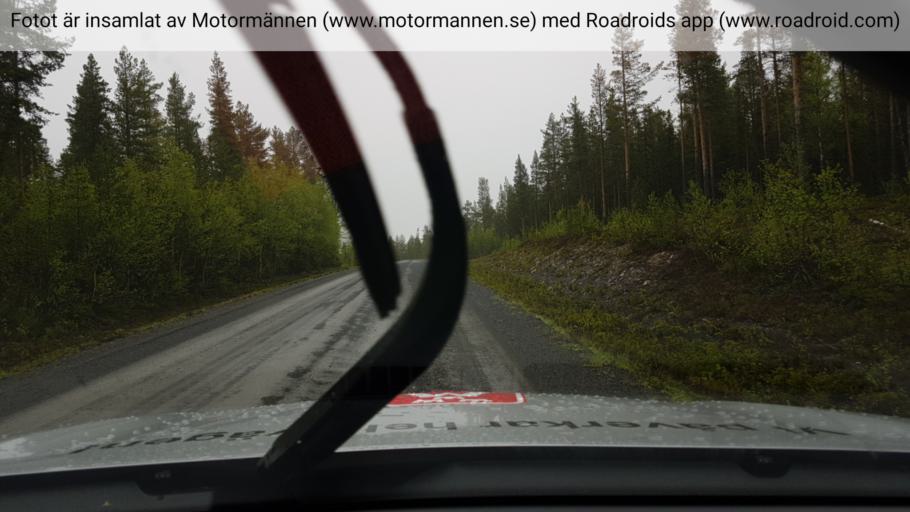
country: SE
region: Jaemtland
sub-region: Krokoms Kommun
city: Valla
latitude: 63.0742
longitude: 13.9599
